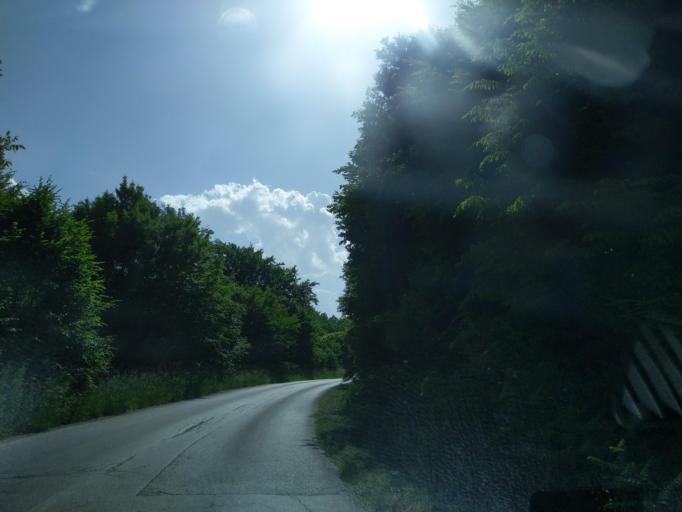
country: RS
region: Central Serbia
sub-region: Zlatiborski Okrug
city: Cajetina
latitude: 43.8709
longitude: 19.7188
